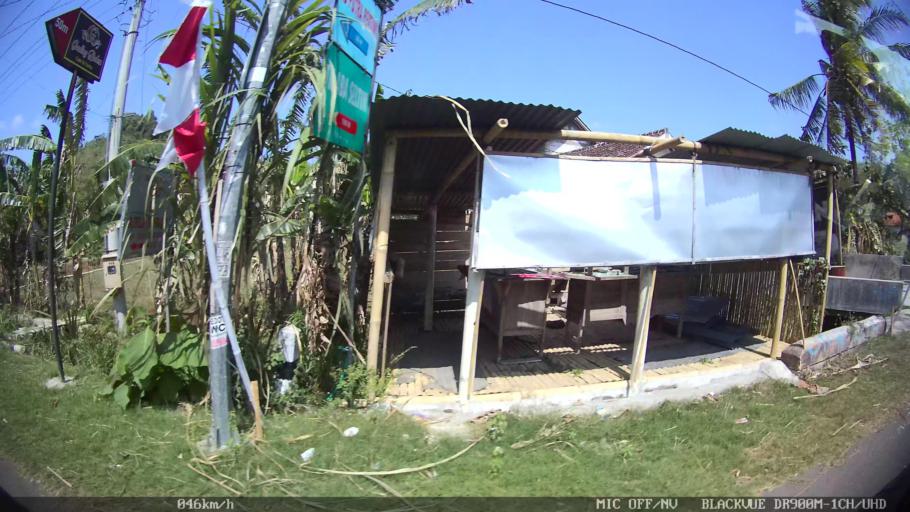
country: ID
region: Daerah Istimewa Yogyakarta
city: Pundong
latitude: -7.9604
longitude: 110.3577
